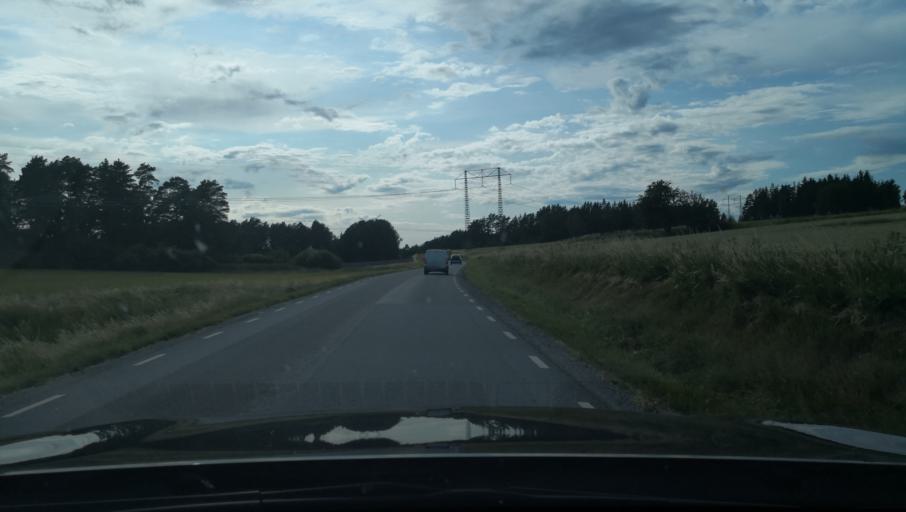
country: SE
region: Uppsala
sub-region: Enkopings Kommun
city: Orsundsbro
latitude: 59.6744
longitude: 17.4280
